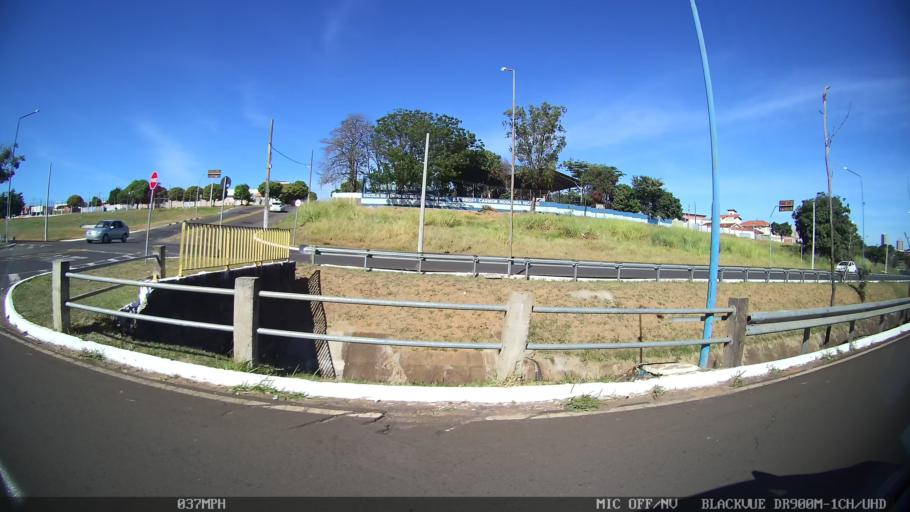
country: BR
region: Sao Paulo
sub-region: Franca
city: Franca
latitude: -20.5201
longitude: -47.3783
